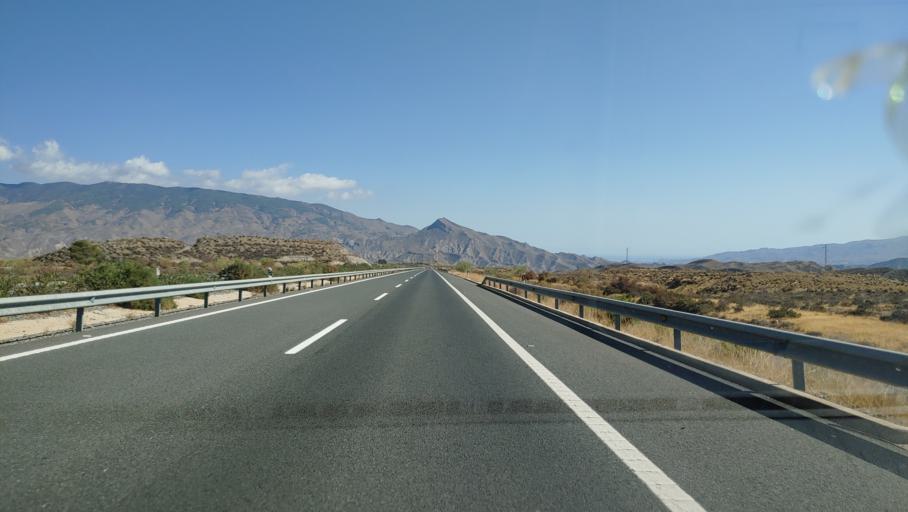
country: ES
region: Andalusia
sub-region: Provincia de Almeria
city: Tabernas
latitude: 37.0491
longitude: -2.4737
